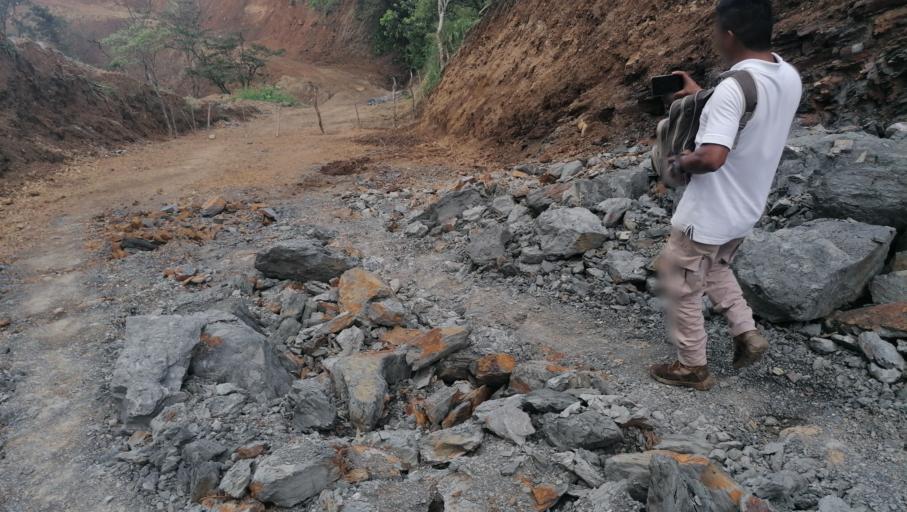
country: MX
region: Chiapas
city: Ostuacan
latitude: 17.3578
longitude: -93.3201
